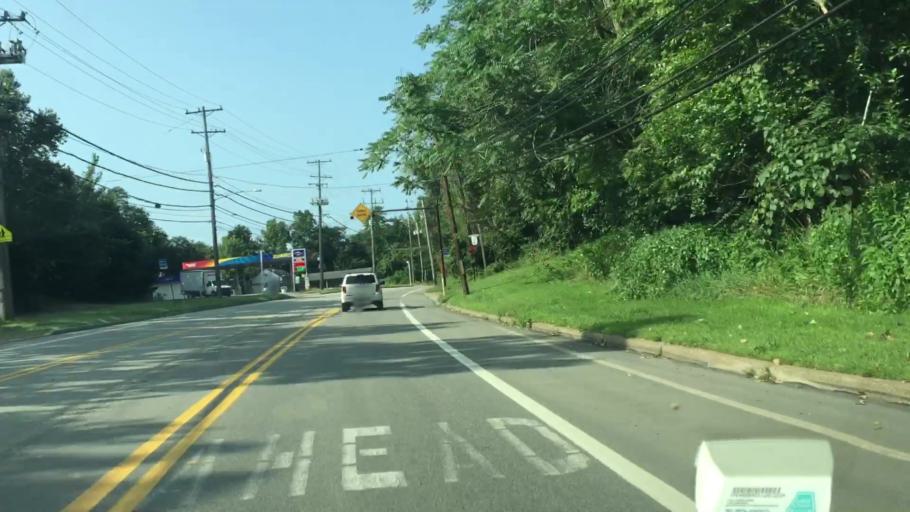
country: US
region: Pennsylvania
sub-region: Allegheny County
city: Blawnox
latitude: 40.5000
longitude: -79.8526
